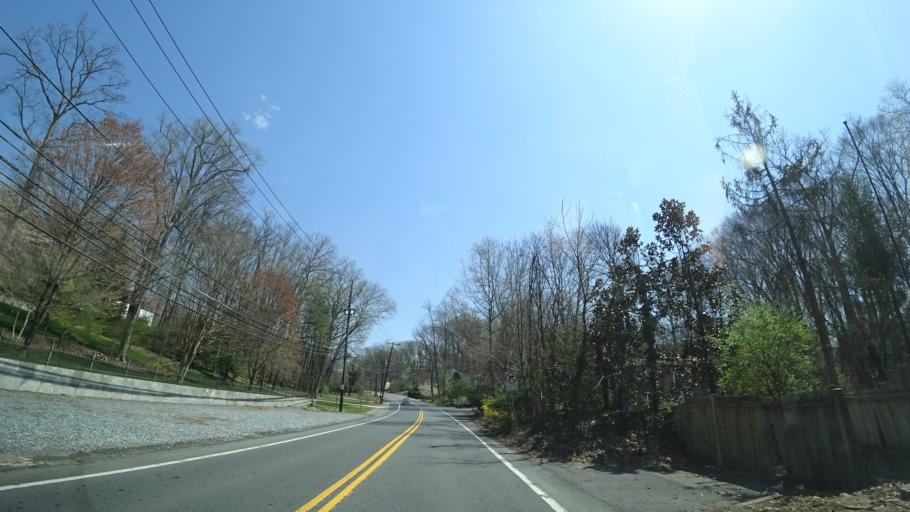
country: US
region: Maryland
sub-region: Montgomery County
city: Bethesda
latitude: 38.9969
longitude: -77.1298
